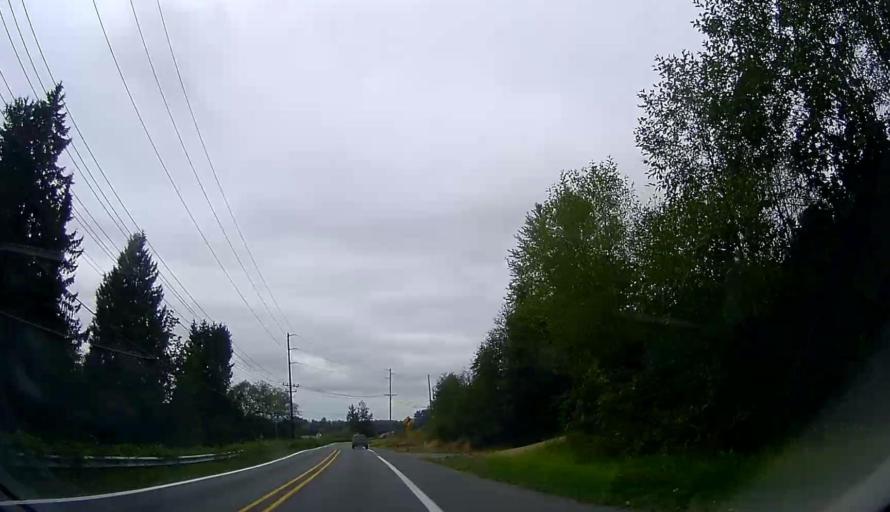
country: US
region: Washington
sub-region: Snohomish County
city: Warm Beach
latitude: 48.2026
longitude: -122.3379
